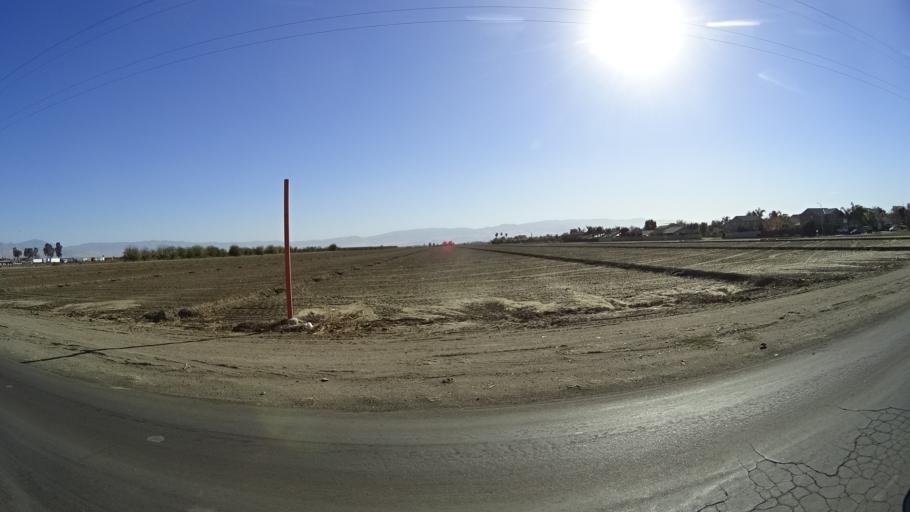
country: US
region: California
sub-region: Kern County
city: Greenfield
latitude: 35.2813
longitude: -118.9985
